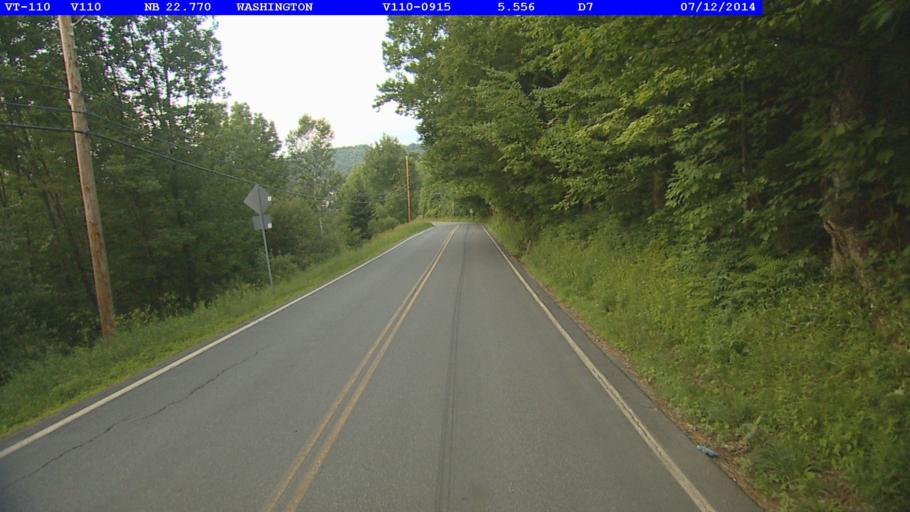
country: US
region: Vermont
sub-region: Washington County
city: South Barre
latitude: 44.1038
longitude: -72.4338
